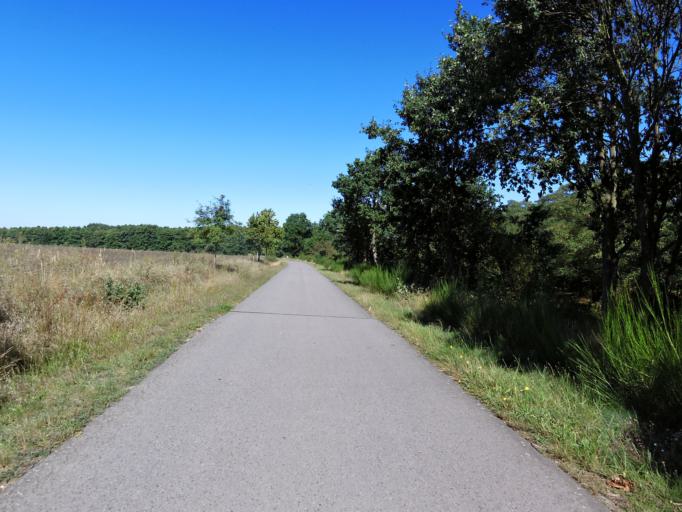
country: DE
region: Saxony-Anhalt
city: Pretzsch
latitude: 51.6719
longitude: 12.8280
